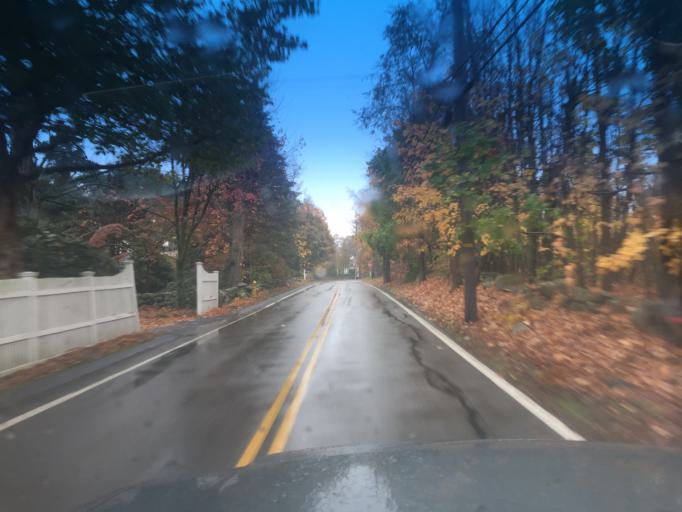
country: US
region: Massachusetts
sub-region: Norfolk County
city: Westwood
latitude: 42.2186
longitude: -71.2024
